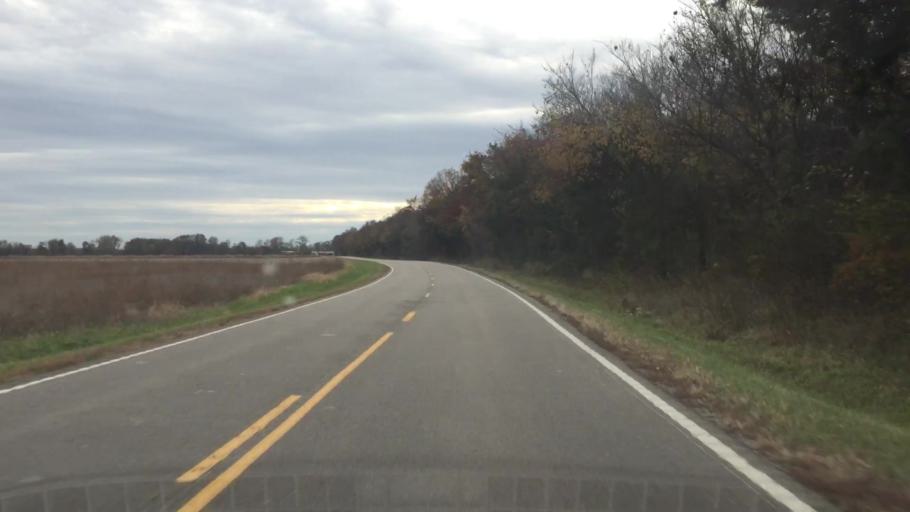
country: US
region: Missouri
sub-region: Callaway County
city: Holts Summit
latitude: 38.6161
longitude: -91.9685
